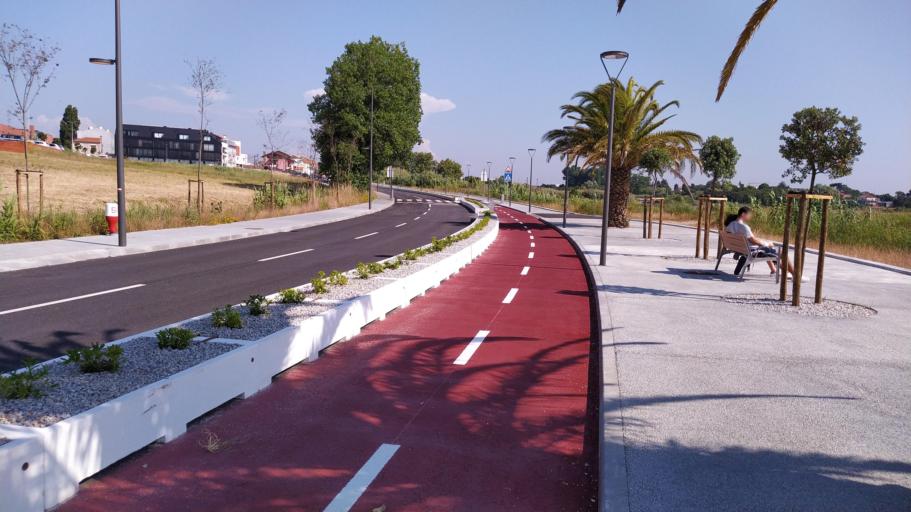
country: PT
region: Aveiro
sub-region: Aveiro
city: Aveiro
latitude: 40.6314
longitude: -8.6619
